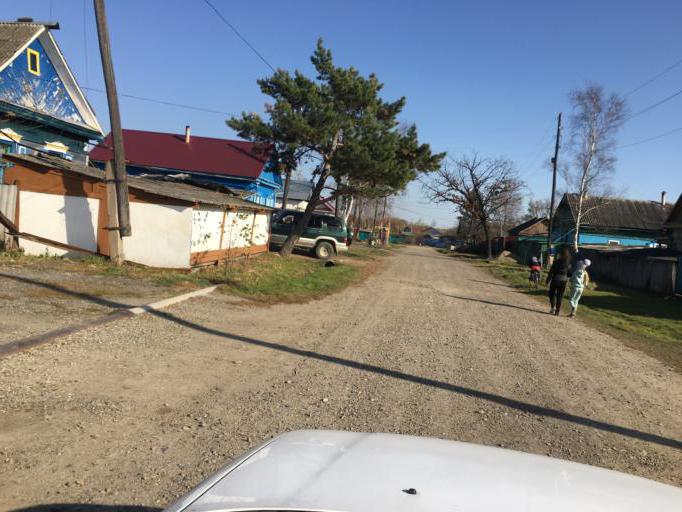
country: RU
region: Primorskiy
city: Dal'nerechensk
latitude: 45.9187
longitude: 133.7147
